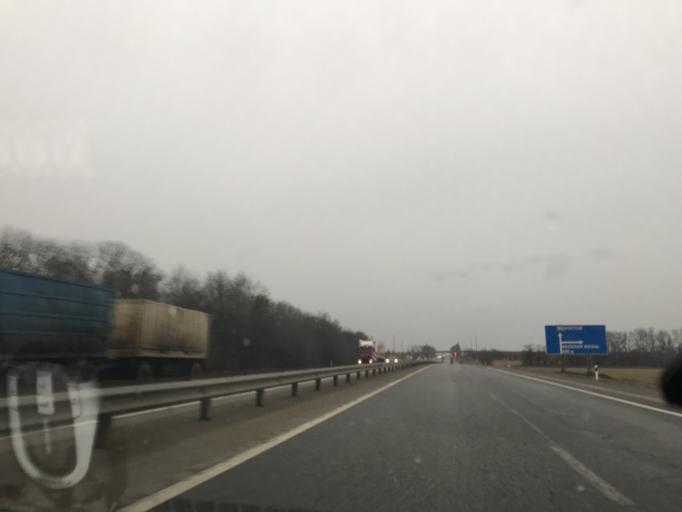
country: RU
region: Krasnodarskiy
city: Pavlovskaya
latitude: 46.2186
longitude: 39.8314
